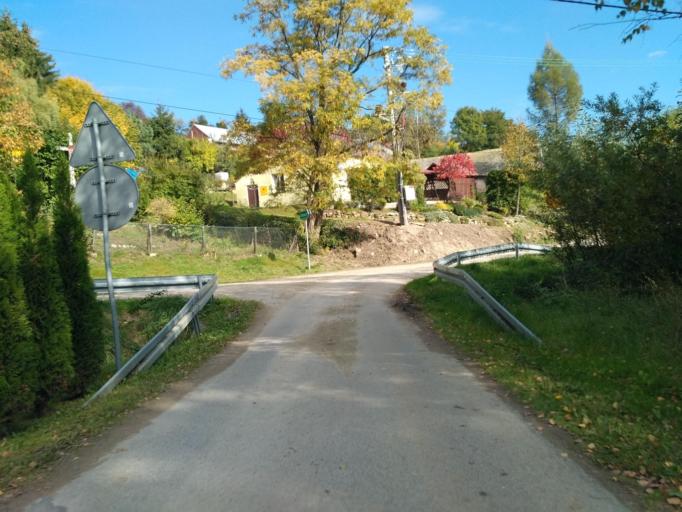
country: PL
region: Subcarpathian Voivodeship
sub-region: Powiat debicki
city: Slotowa
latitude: 49.9222
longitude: 21.2983
